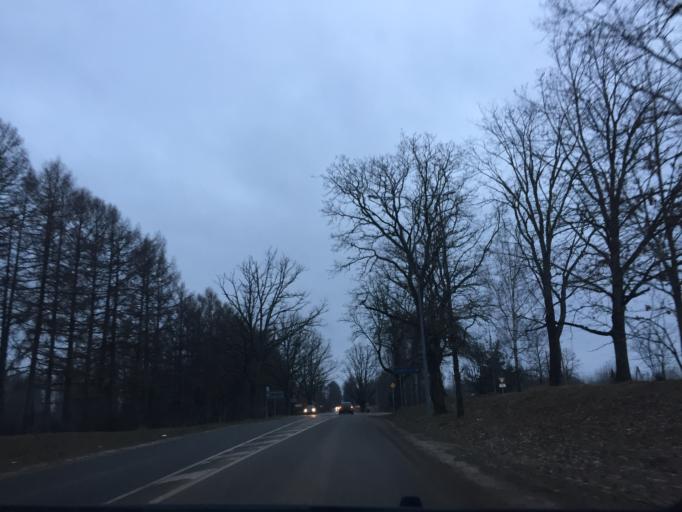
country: LV
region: Cesu Rajons
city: Cesis
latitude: 57.2958
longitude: 25.2685
